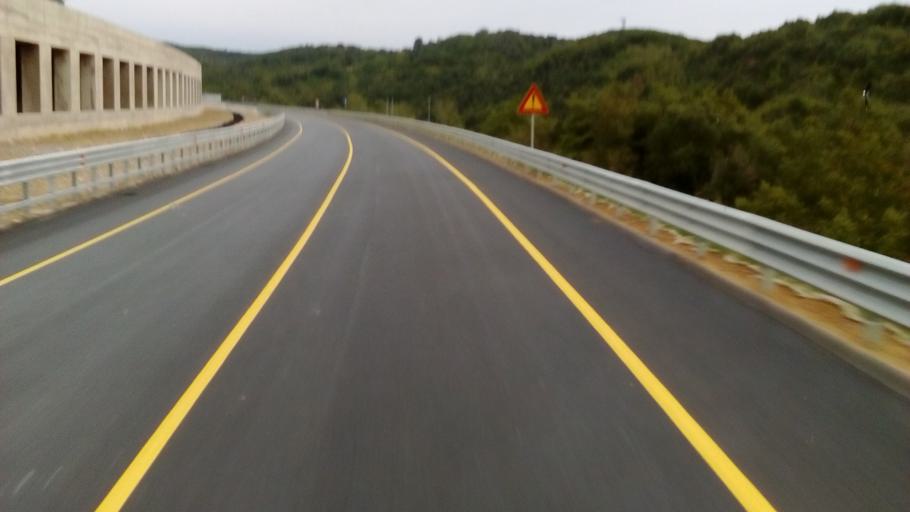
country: IT
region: Tuscany
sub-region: Provincia di Grosseto
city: Civitella Marittima
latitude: 43.0430
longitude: 11.2854
